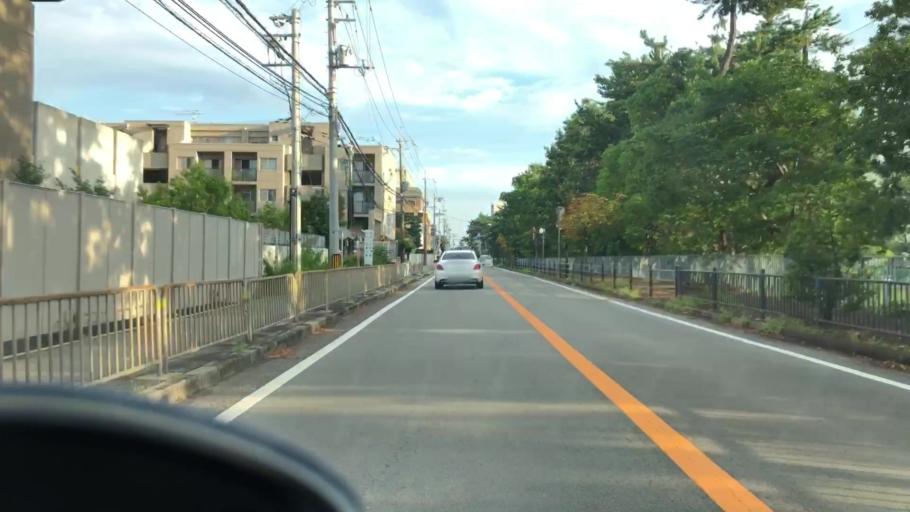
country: JP
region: Hyogo
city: Takarazuka
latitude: 34.7788
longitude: 135.3711
